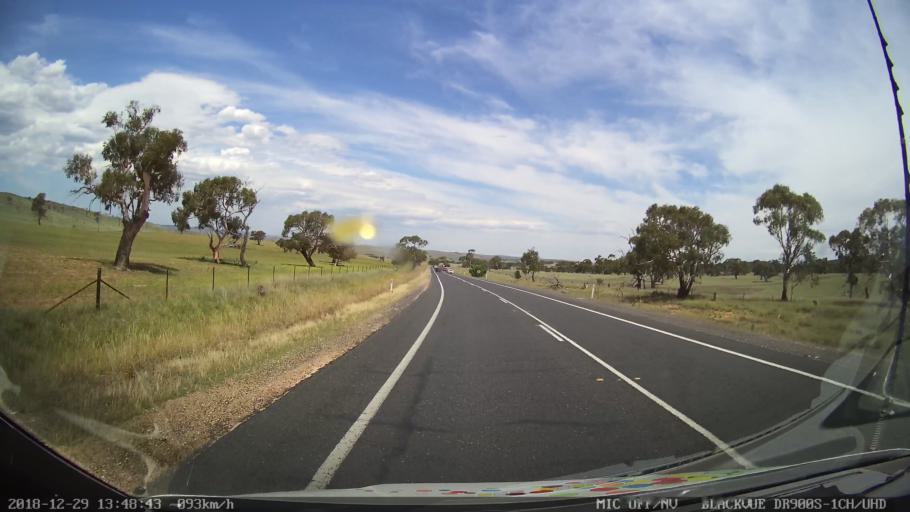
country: AU
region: New South Wales
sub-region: Cooma-Monaro
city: Cooma
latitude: -36.1439
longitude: 149.1490
